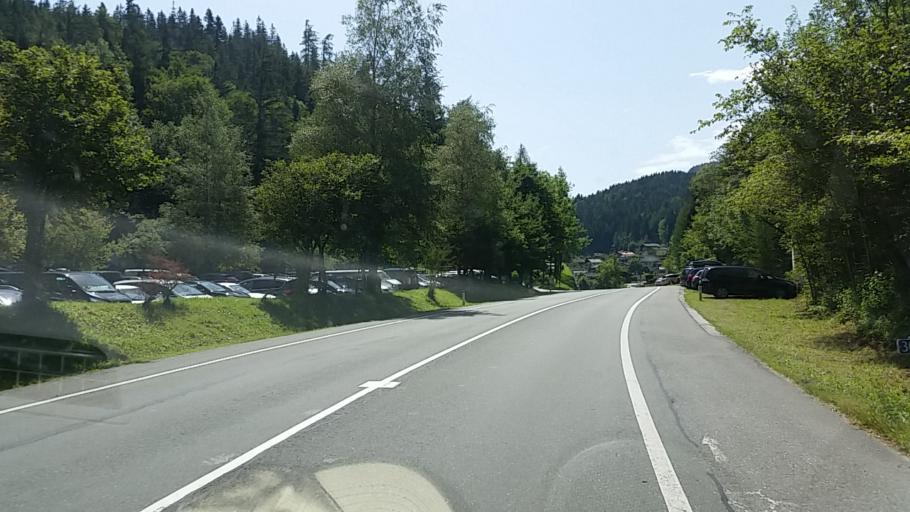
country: AT
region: Salzburg
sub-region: Politischer Bezirk Sankt Johann im Pongau
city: Werfen
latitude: 47.4837
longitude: 13.1854
